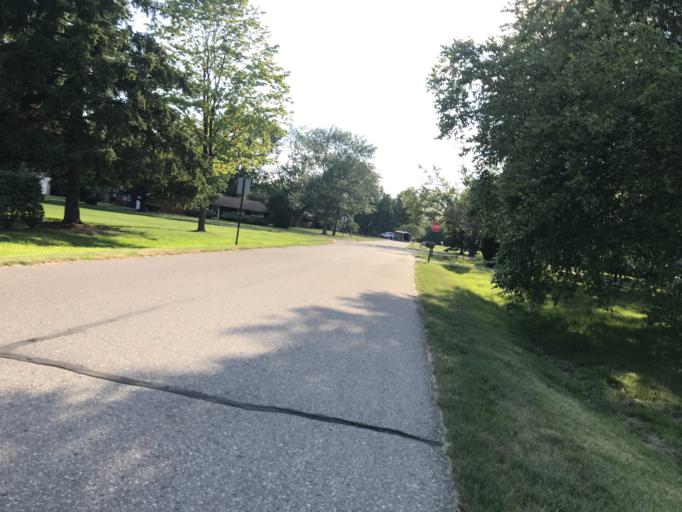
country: US
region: Michigan
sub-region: Oakland County
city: Farmington
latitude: 42.4693
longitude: -83.3241
